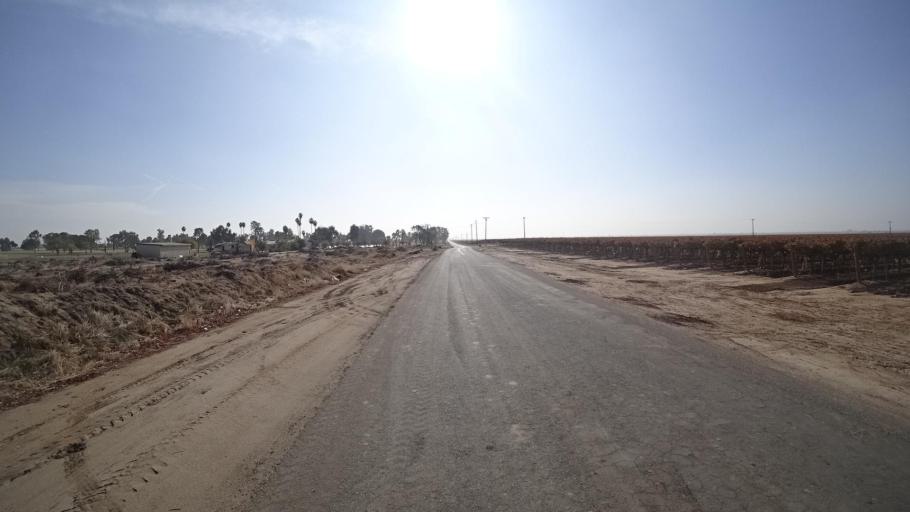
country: US
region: California
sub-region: Kern County
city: Greenacres
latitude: 35.5225
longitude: -119.1161
